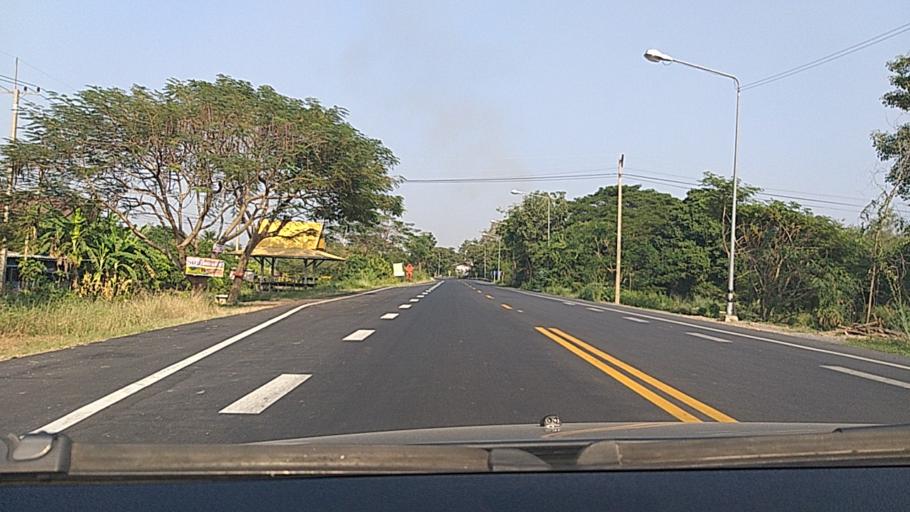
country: TH
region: Sing Buri
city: Phrom Buri
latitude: 14.7604
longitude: 100.4362
